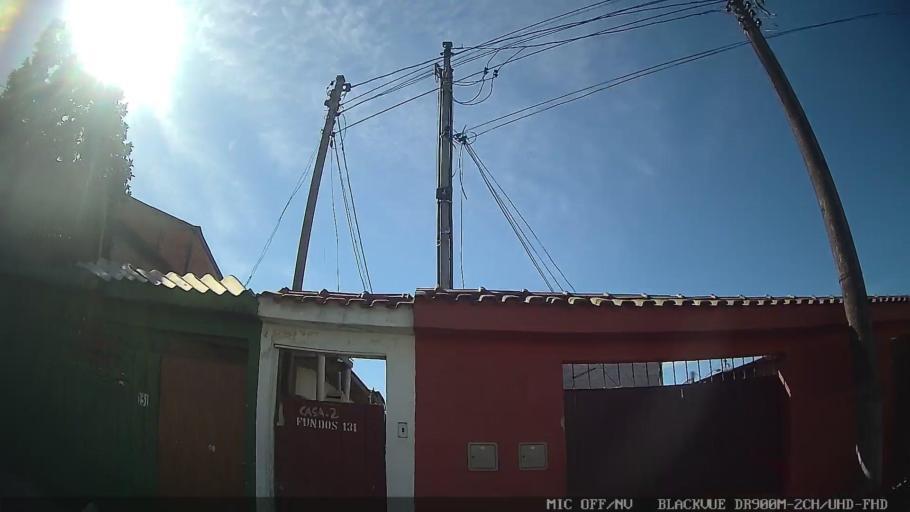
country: BR
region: Sao Paulo
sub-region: Santos
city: Santos
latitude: -23.9444
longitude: -46.2912
